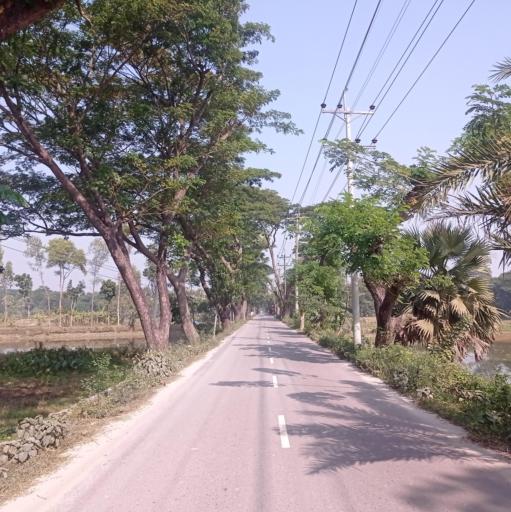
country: BD
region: Dhaka
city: Narsingdi
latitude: 24.0550
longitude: 90.6843
